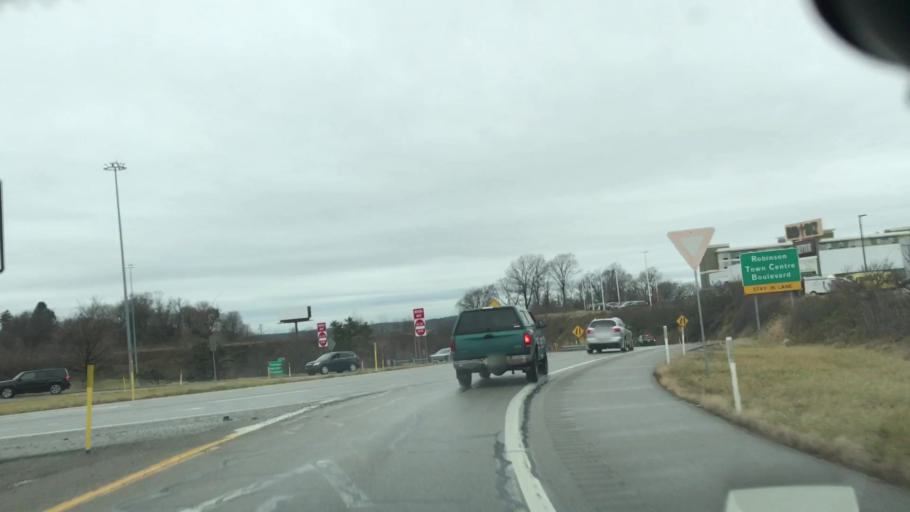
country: US
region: Pennsylvania
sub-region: Allegheny County
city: Oakdale
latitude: 40.4480
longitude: -80.1643
